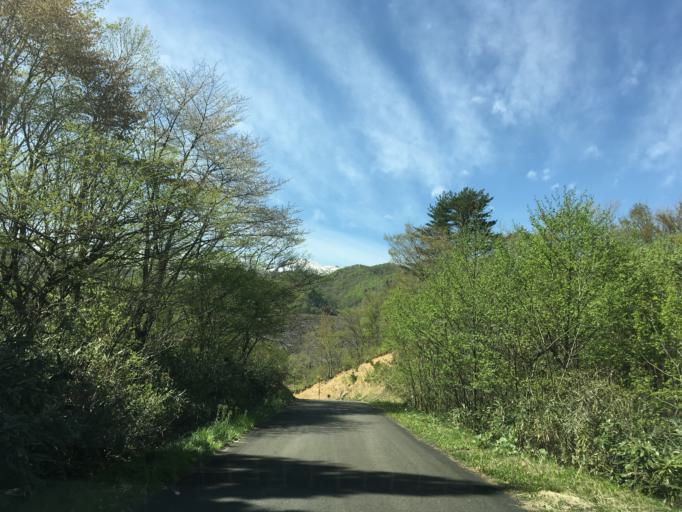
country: JP
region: Iwate
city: Mizusawa
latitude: 39.1181
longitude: 140.9237
